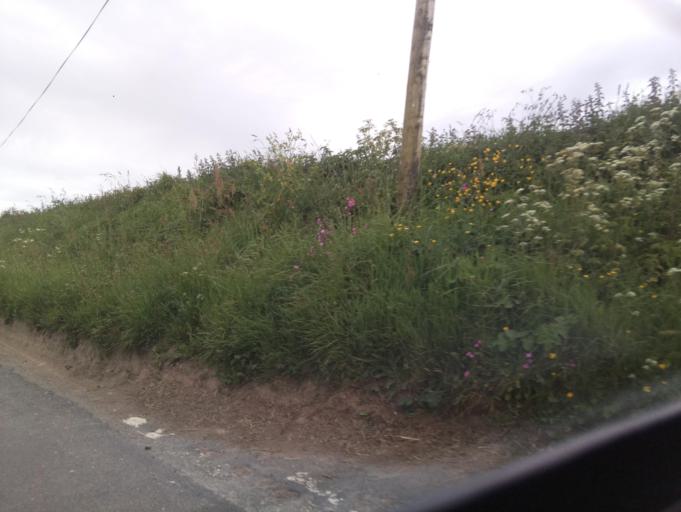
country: GB
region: England
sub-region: Devon
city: Dartmouth
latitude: 50.3207
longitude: -3.6365
